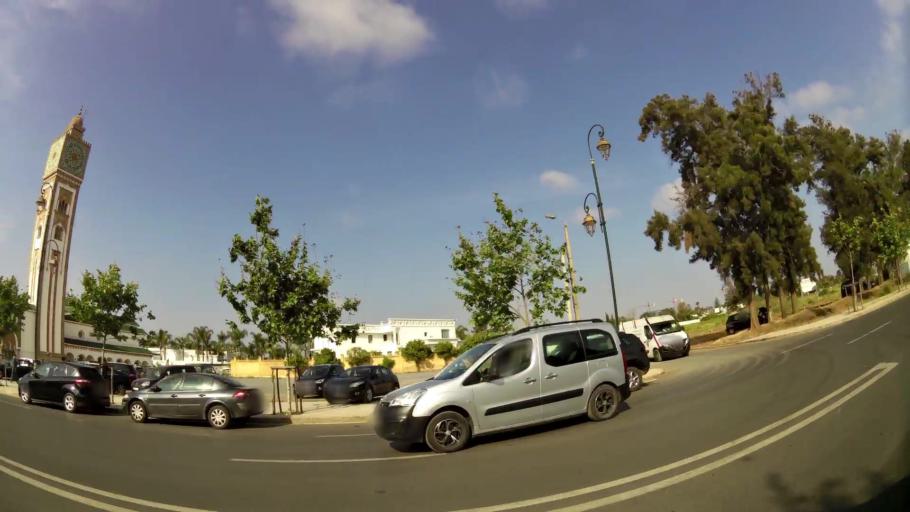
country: MA
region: Rabat-Sale-Zemmour-Zaer
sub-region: Rabat
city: Rabat
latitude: 33.9588
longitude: -6.8186
